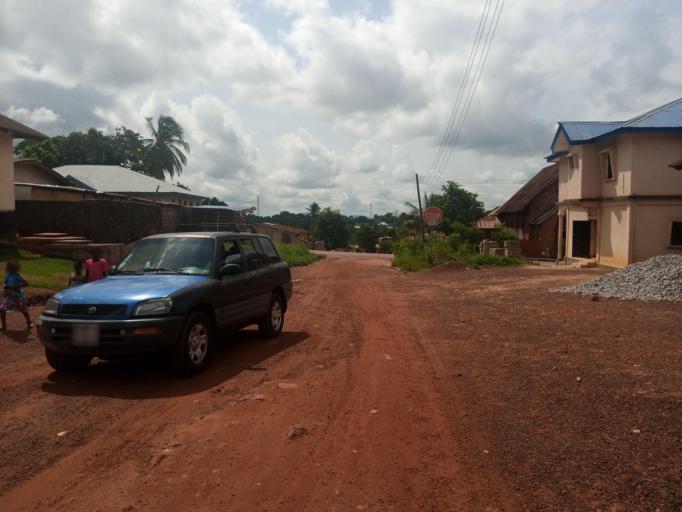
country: SL
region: Southern Province
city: Bo
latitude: 7.9711
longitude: -11.7405
